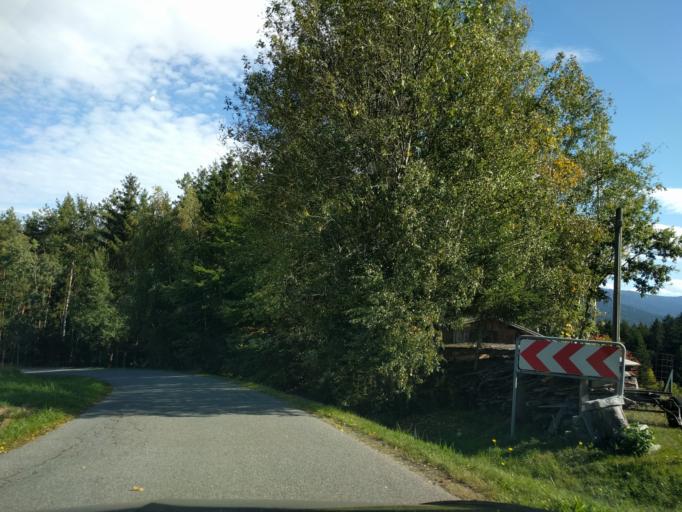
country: DE
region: Bavaria
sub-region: Upper Palatinate
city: Kotzting
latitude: 49.1494
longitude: 12.8906
